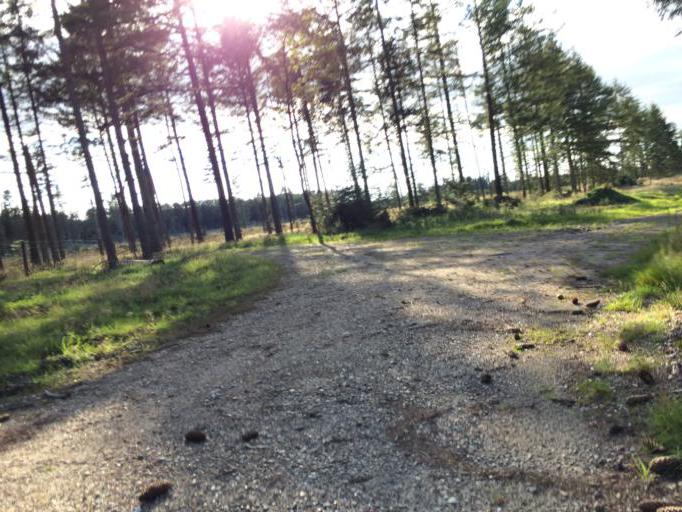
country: DK
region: Central Jutland
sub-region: Holstebro Kommune
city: Ulfborg
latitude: 56.2660
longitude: 8.4391
